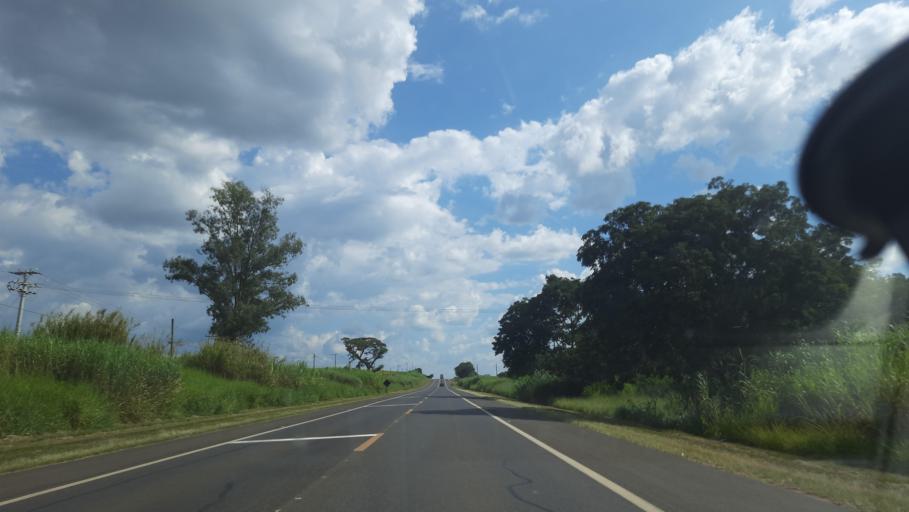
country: BR
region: Sao Paulo
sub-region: Sao Jose Do Rio Pardo
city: Sao Jose do Rio Pardo
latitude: -21.6703
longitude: -46.9221
